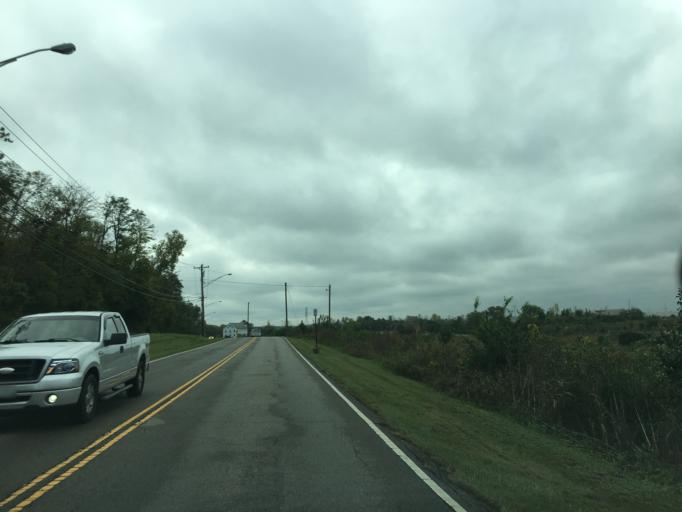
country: US
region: Ohio
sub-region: Butler County
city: Beckett Ridge
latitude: 39.3470
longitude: -84.4470
